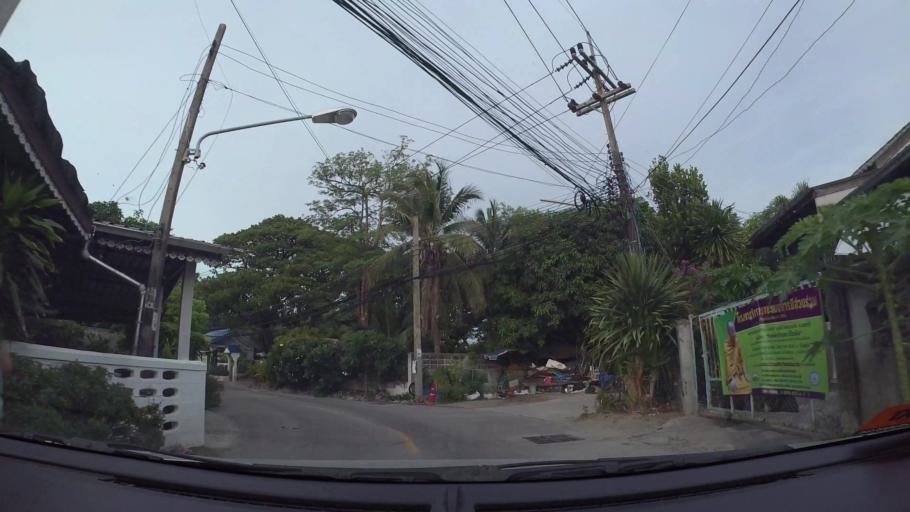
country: TH
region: Chon Buri
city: Chon Buri
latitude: 13.3411
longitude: 100.9813
